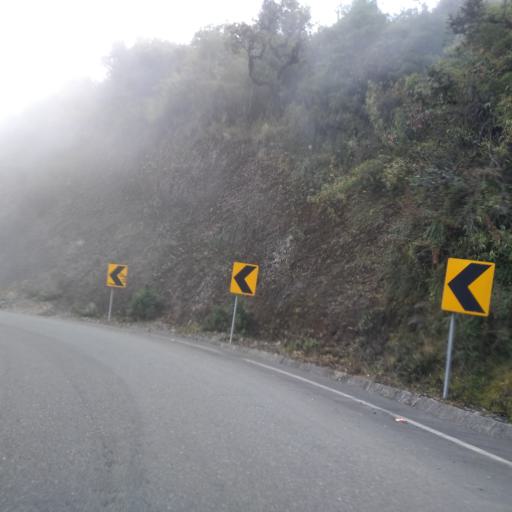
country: EC
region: Cotopaxi
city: La Mana
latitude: -0.9876
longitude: -78.9754
